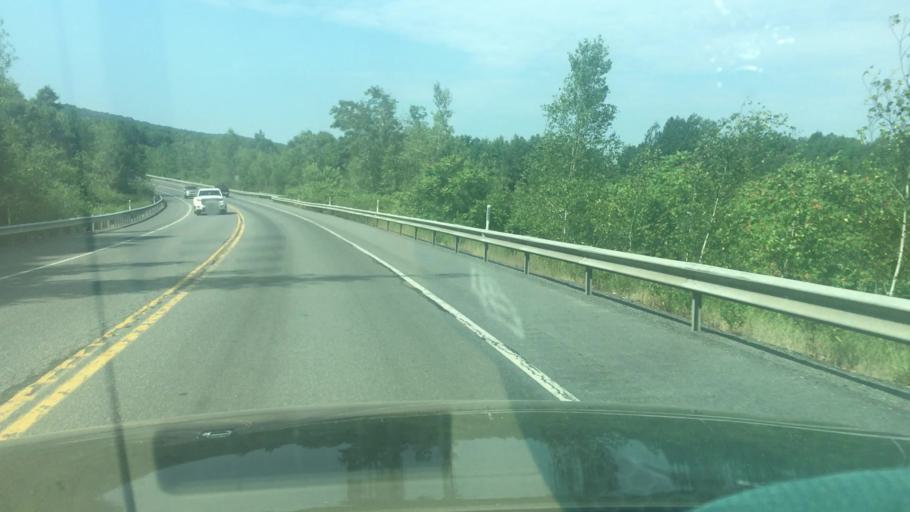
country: US
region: Pennsylvania
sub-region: Northumberland County
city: Kulpmont
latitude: 40.7896
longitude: -76.4451
